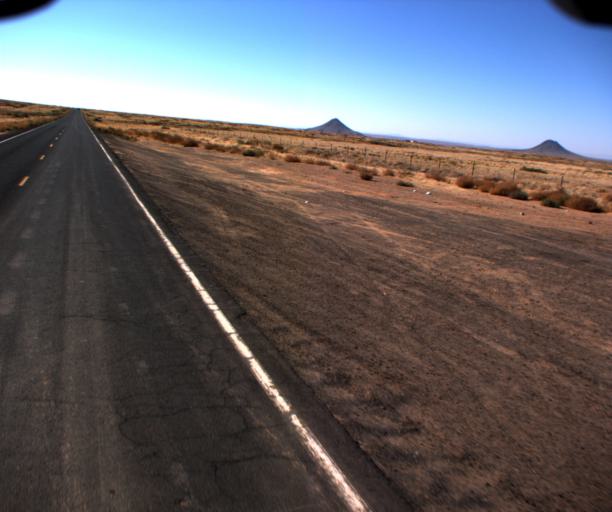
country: US
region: Arizona
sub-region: Navajo County
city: Dilkon
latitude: 35.4309
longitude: -110.4255
